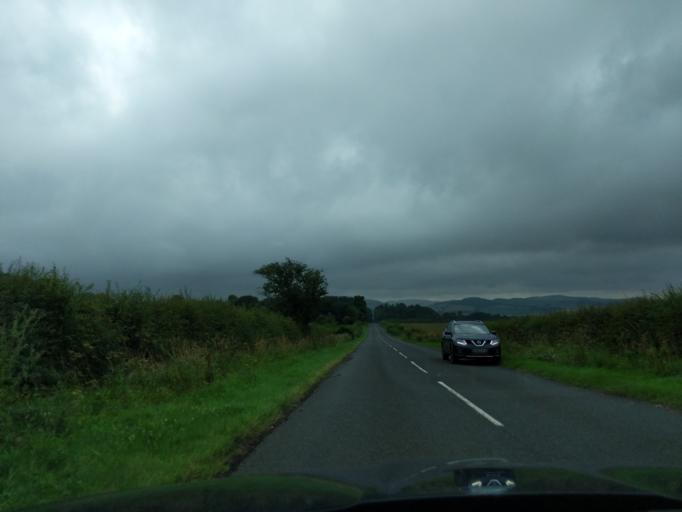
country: GB
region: England
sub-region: Northumberland
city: Ford
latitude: 55.6378
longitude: -2.0701
